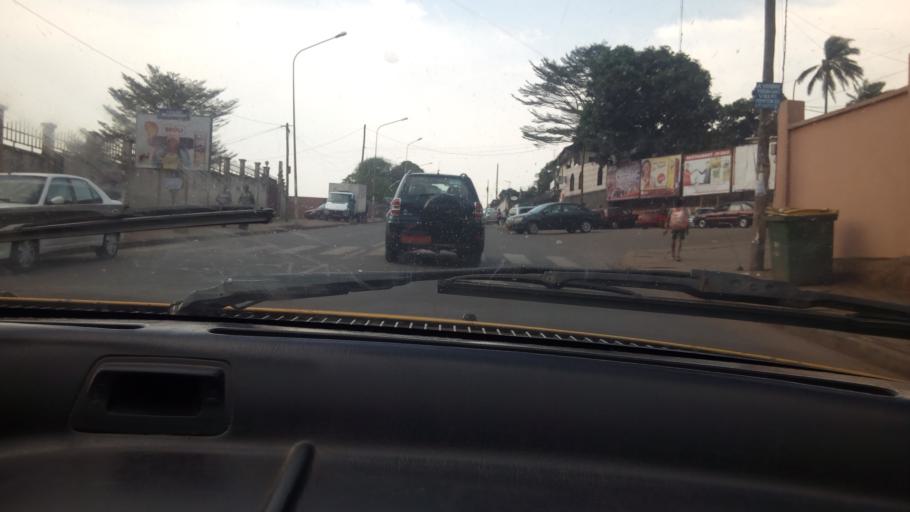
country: CM
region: Centre
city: Yaounde
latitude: 3.8723
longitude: 11.5160
